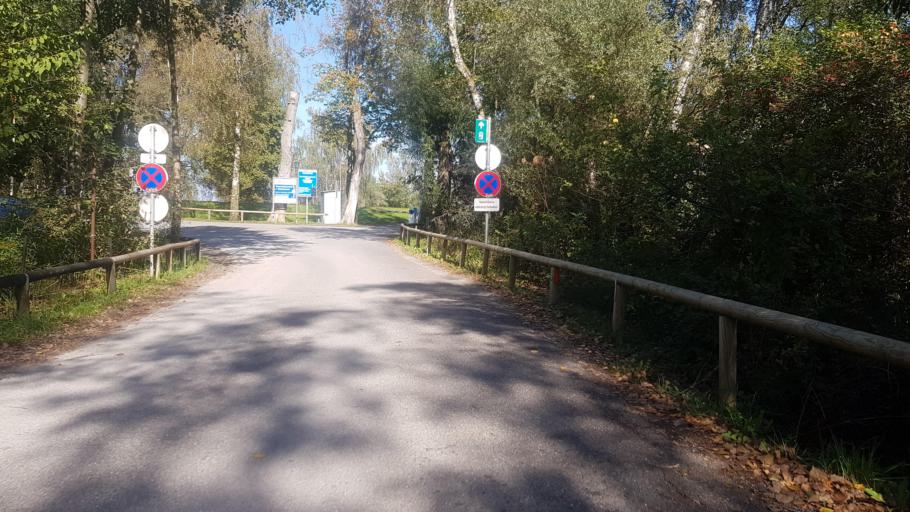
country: AT
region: Vorarlberg
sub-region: Politischer Bezirk Bregenz
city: Hochst
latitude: 47.4953
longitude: 9.6280
